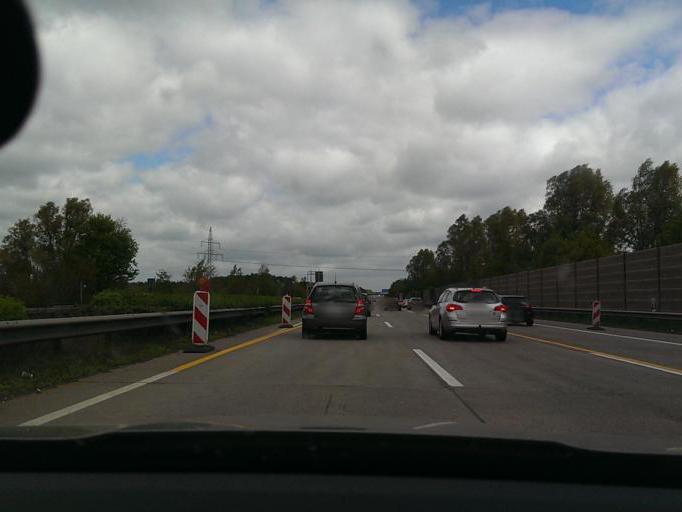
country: DE
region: Lower Saxony
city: Essel
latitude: 52.6871
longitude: 9.6890
